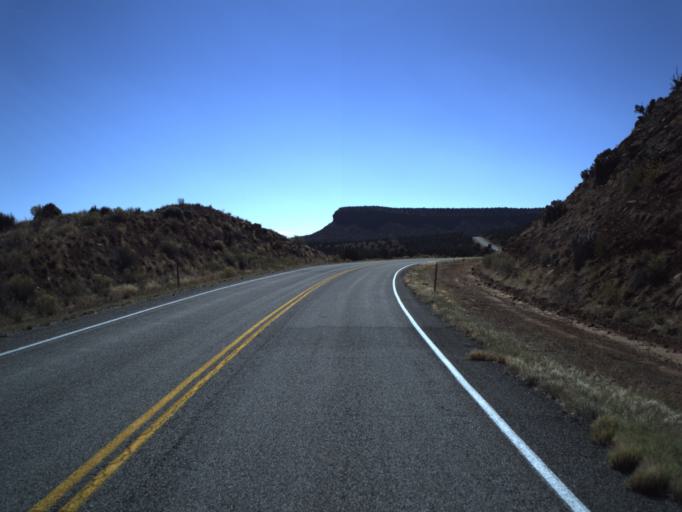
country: US
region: Utah
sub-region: San Juan County
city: Blanding
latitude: 37.5869
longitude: -110.0401
